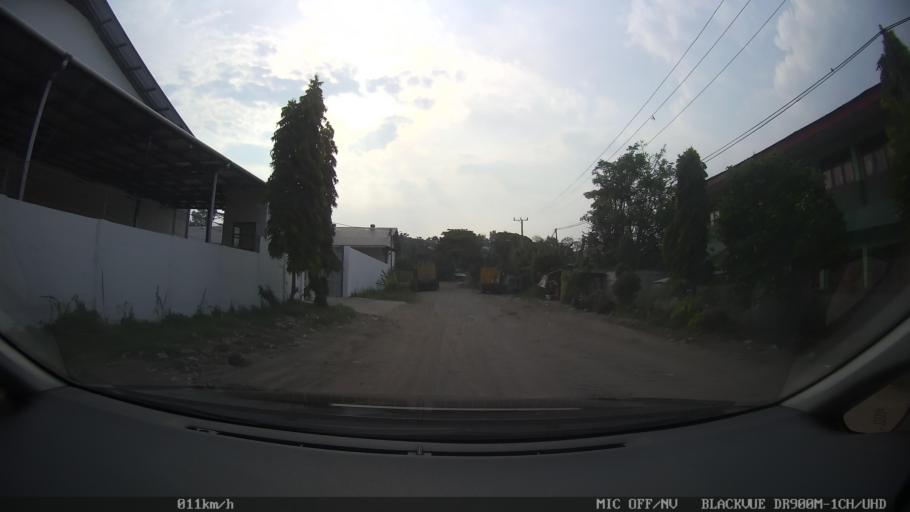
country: ID
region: Lampung
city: Panjang
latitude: -5.4461
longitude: 105.3083
